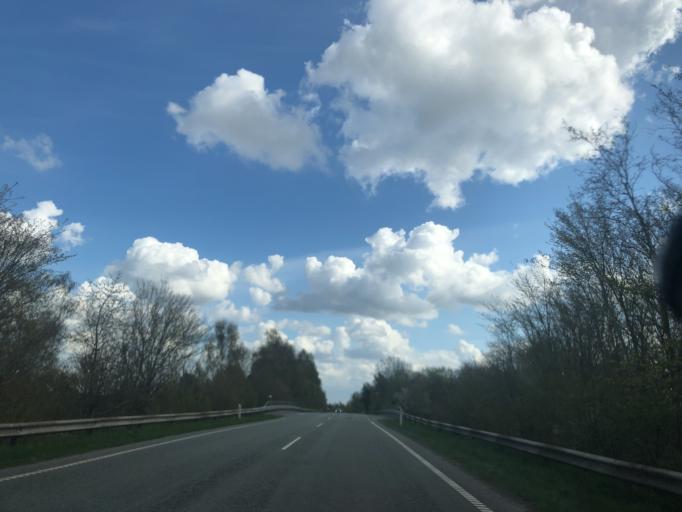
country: DK
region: Capital Region
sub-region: Gribskov Kommune
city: Helsinge
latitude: 56.0214
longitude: 12.1803
